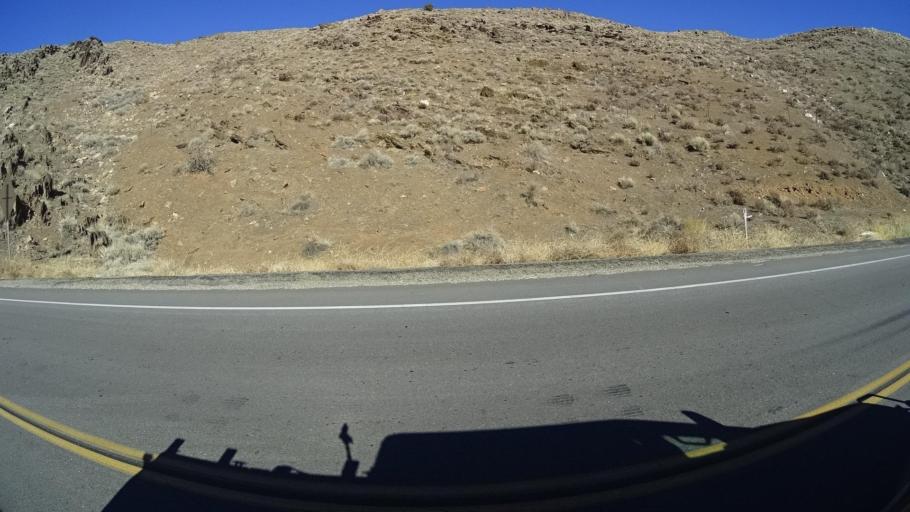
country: US
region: California
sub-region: Kern County
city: Wofford Heights
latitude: 35.6760
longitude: -118.4022
